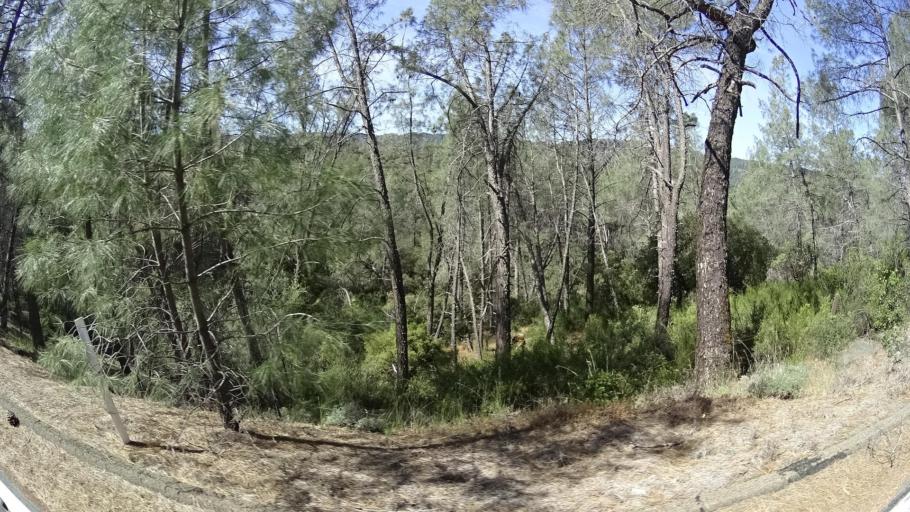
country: US
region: California
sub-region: Lake County
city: Cobb
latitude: 38.8751
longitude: -122.7738
